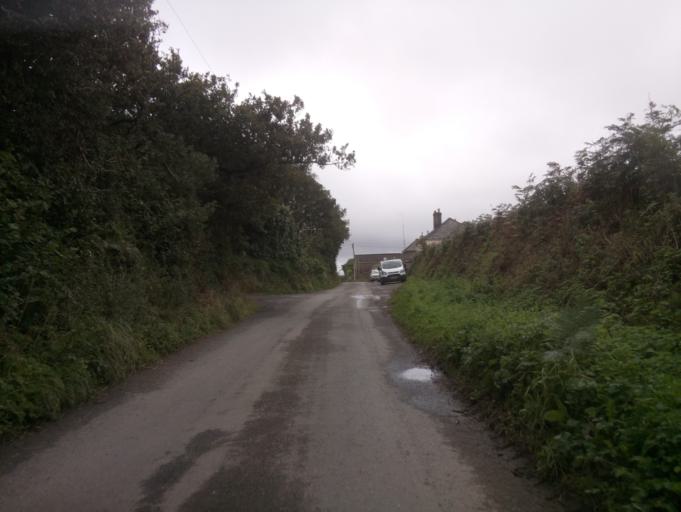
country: GB
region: England
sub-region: Devon
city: Kingsbridge
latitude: 50.3099
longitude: -3.7160
